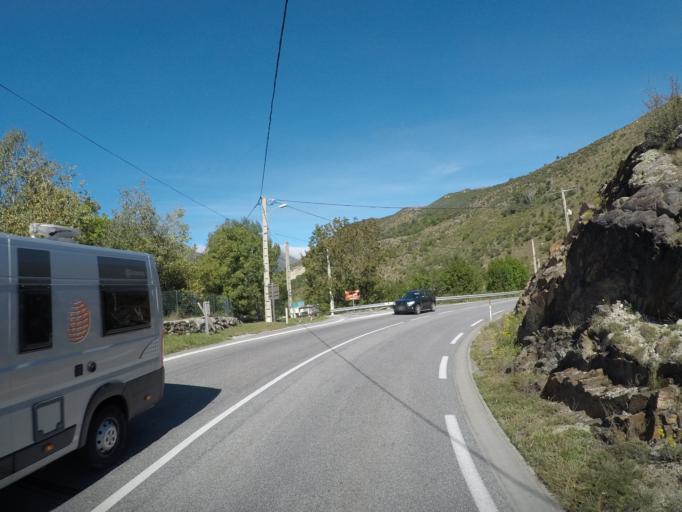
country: ES
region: Catalonia
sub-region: Provincia de Girona
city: Guils de Cerdanya
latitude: 42.4696
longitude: 1.8823
